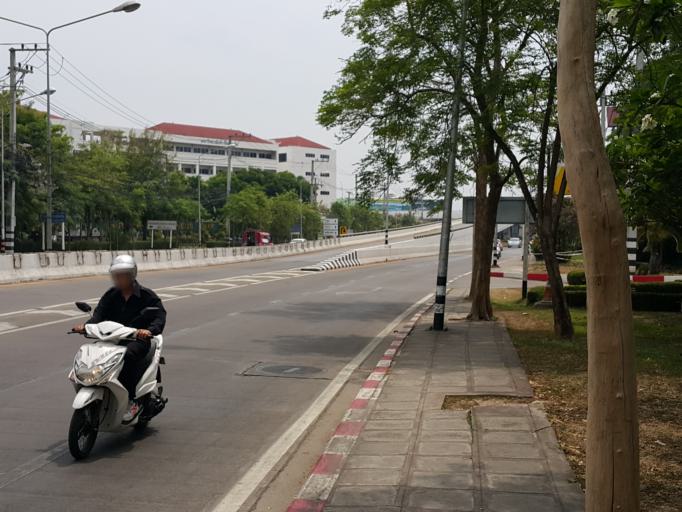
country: TH
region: Chiang Mai
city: Chiang Mai
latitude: 18.7713
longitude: 98.9731
